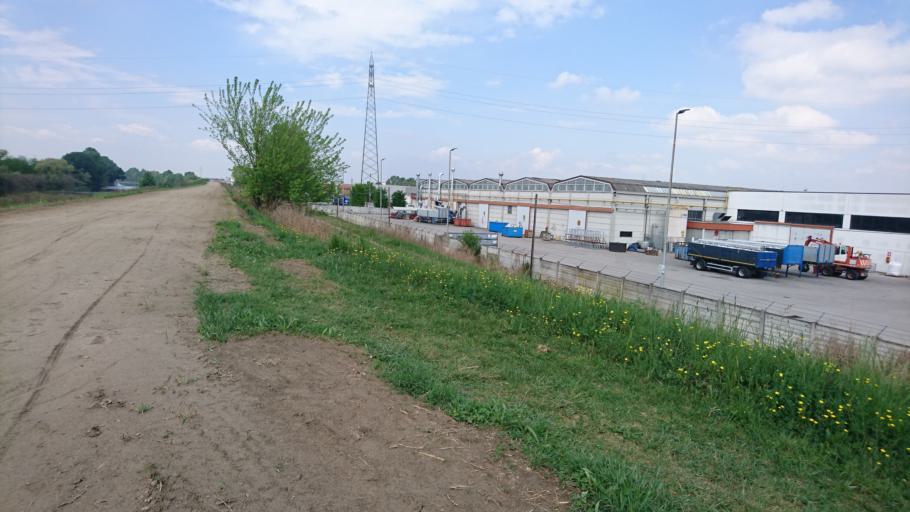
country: IT
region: Veneto
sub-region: Provincia di Padova
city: Oltre Brenta
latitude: 45.4172
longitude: 11.9853
